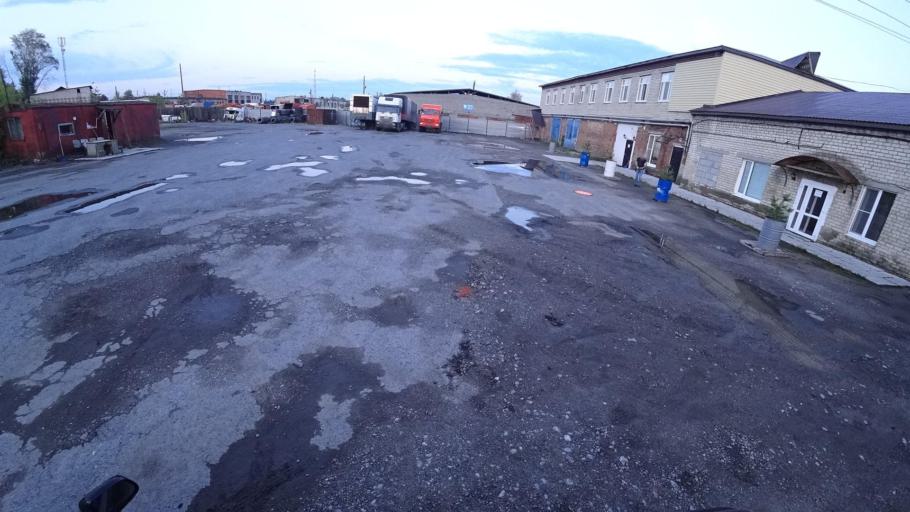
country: RU
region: Sverdlovsk
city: Kamyshlov
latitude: 56.8494
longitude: 62.7352
